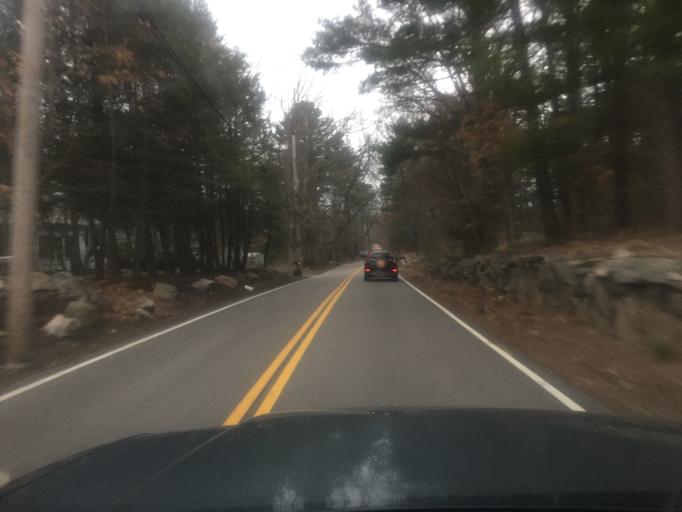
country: US
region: Massachusetts
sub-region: Norfolk County
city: Medway
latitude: 42.1455
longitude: -71.4350
